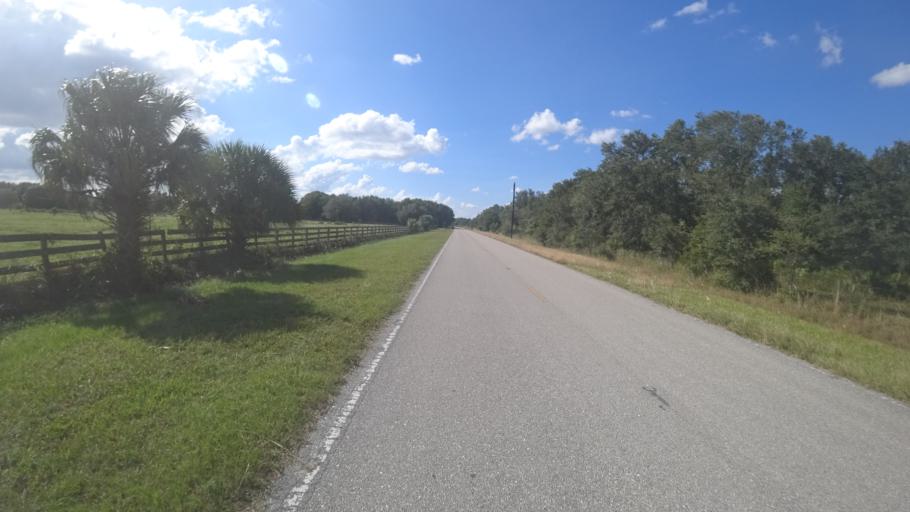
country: US
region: Florida
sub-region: DeSoto County
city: Nocatee
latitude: 27.2721
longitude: -82.1037
